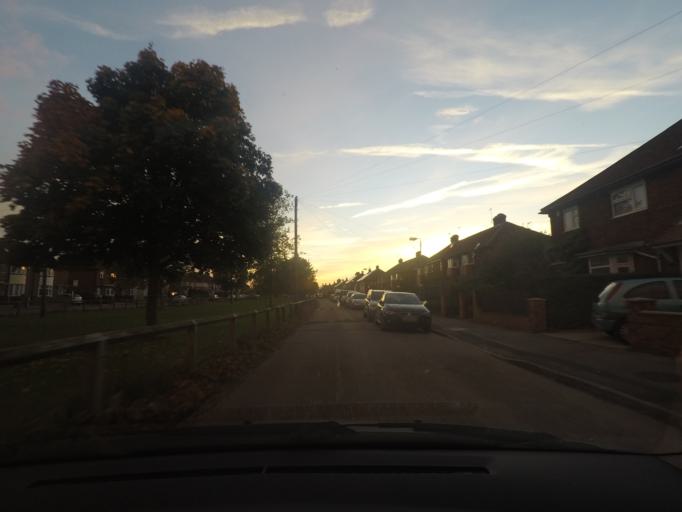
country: GB
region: England
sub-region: City of York
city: York
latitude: 53.9784
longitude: -1.0869
